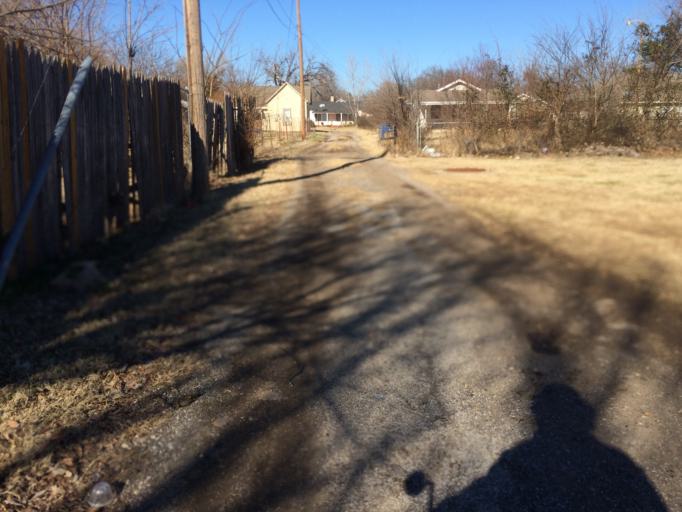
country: US
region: Oklahoma
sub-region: Cleveland County
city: Norman
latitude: 35.2224
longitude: -97.4312
